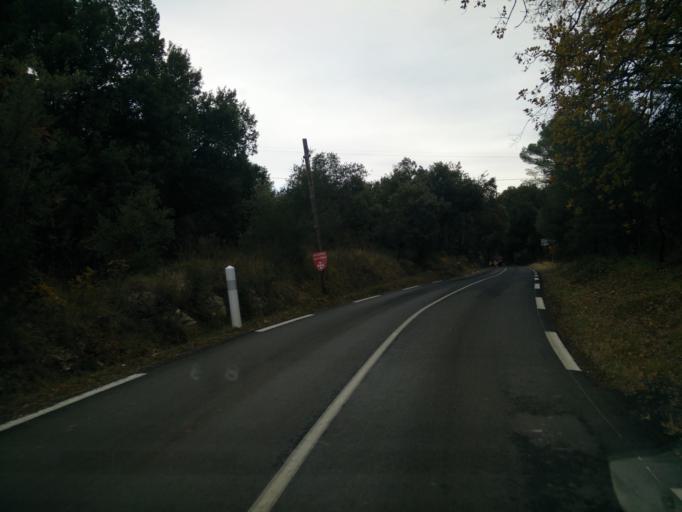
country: FR
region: Provence-Alpes-Cote d'Azur
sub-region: Departement du Var
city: Le Val
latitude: 43.4633
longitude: 6.1085
